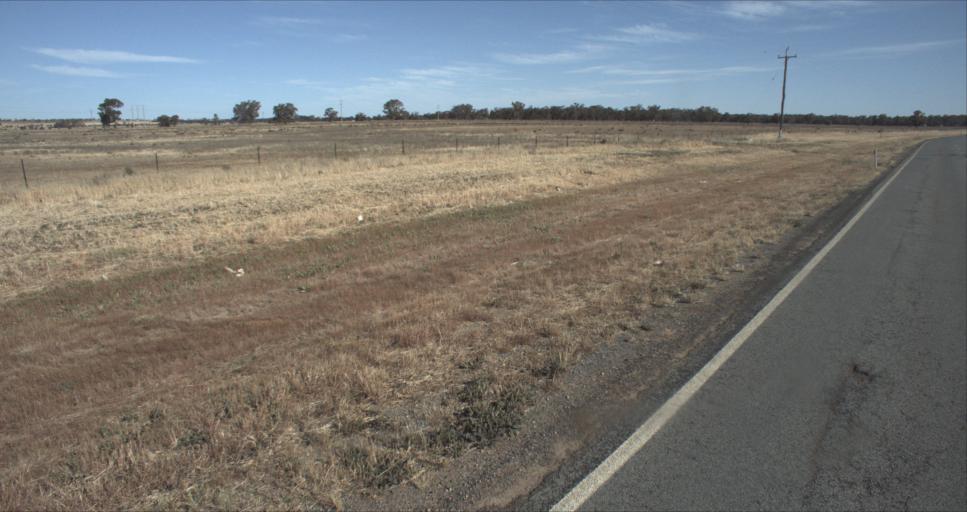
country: AU
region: New South Wales
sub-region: Leeton
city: Leeton
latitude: -34.6123
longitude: 146.4034
